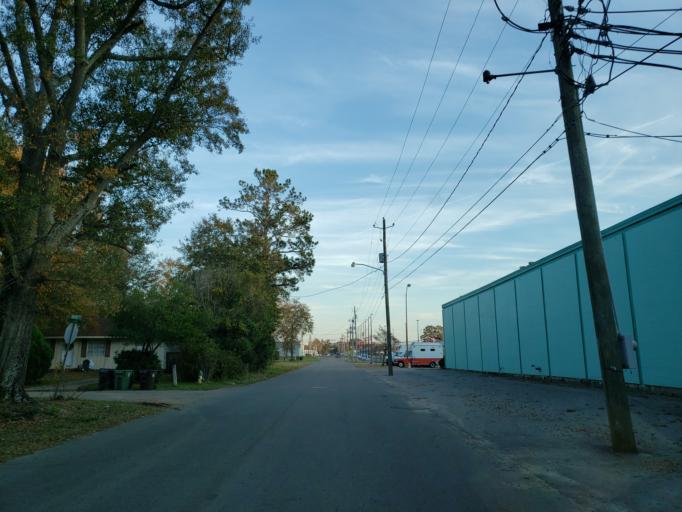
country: US
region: Mississippi
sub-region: Forrest County
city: Hattiesburg
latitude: 31.3154
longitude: -89.3110
